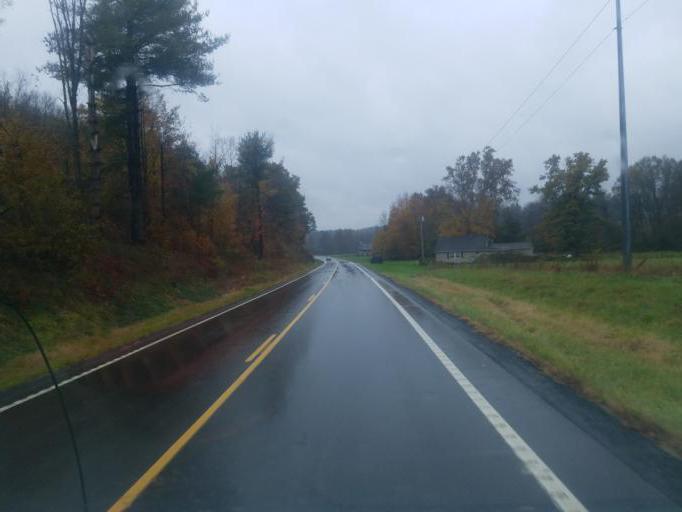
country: US
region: Ohio
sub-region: Muskingum County
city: Frazeysburg
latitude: 40.1804
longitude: -82.2297
